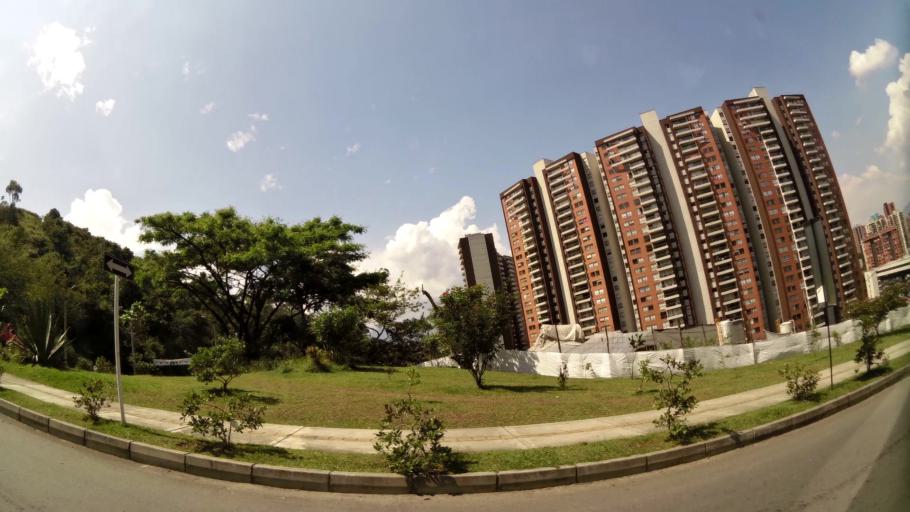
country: CO
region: Antioquia
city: Itagui
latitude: 6.2157
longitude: -75.6062
